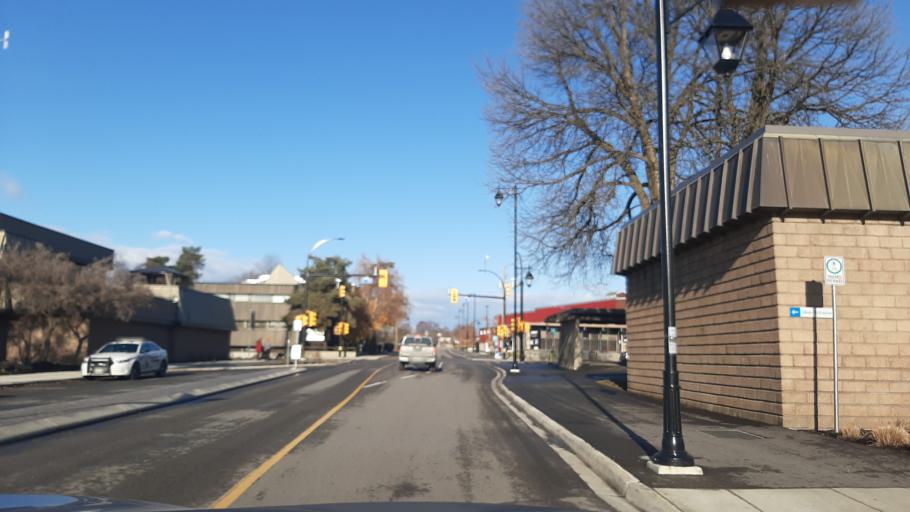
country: CA
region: British Columbia
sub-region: Regional District of North Okanagan
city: Vernon
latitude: 50.2668
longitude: -119.2708
